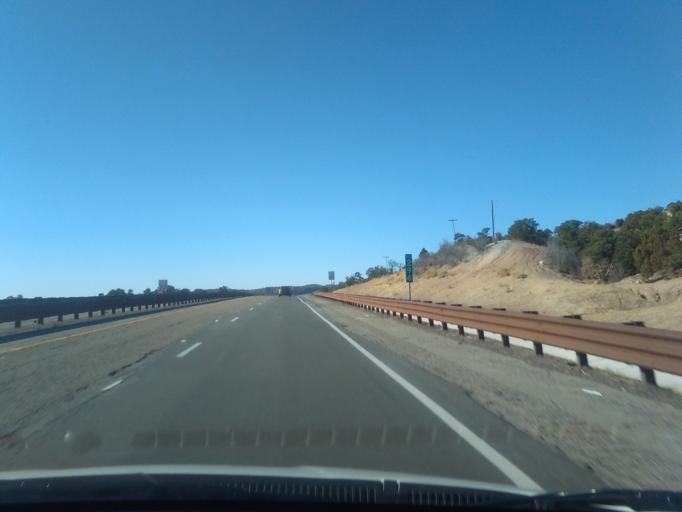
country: US
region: New Mexico
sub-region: Santa Fe County
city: Eldorado at Santa Fe
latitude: 35.5475
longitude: -105.8287
